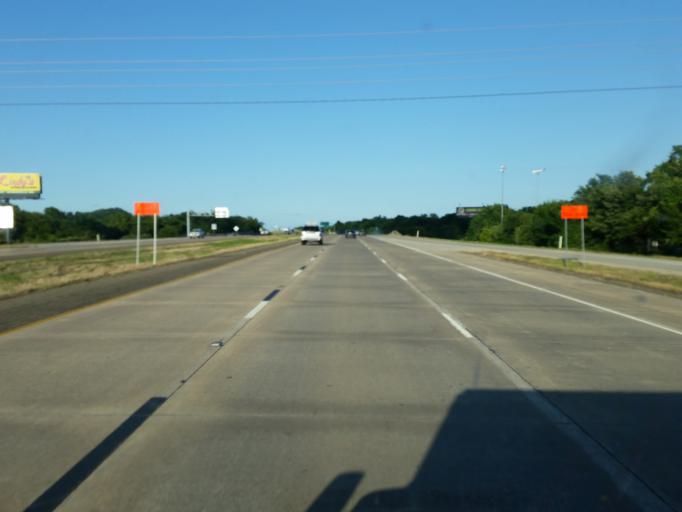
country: US
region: Texas
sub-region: Dallas County
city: Balch Springs
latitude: 32.7018
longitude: -96.6182
